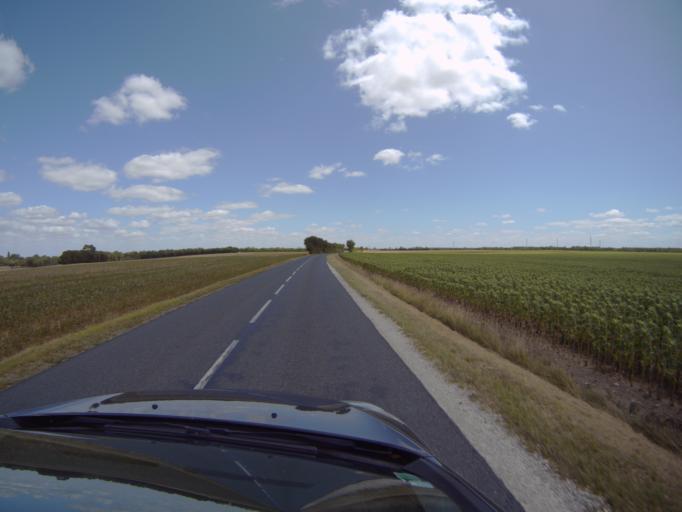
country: FR
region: Poitou-Charentes
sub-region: Departement de la Charente-Maritime
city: Saint-Jean-de-Liversay
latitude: 46.2605
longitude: -0.8606
